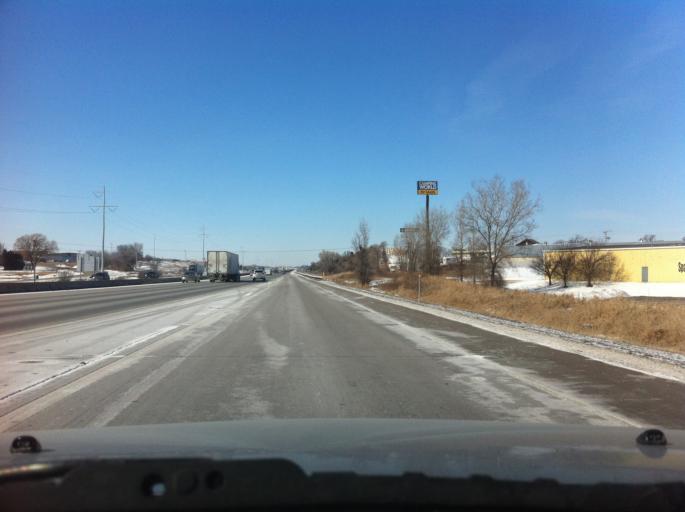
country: US
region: Wisconsin
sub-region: Dane County
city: Windsor
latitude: 43.1816
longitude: -89.3276
